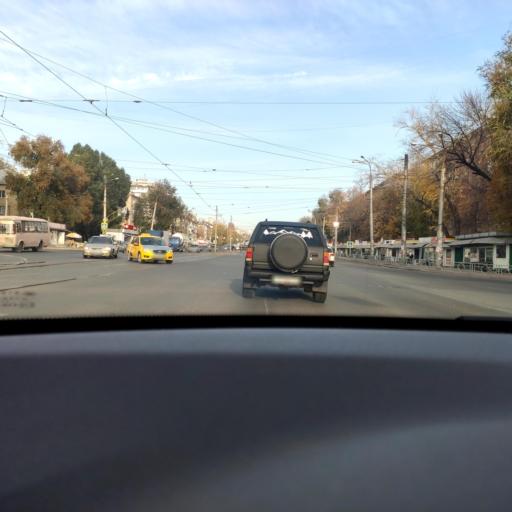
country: RU
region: Samara
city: Samara
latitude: 53.2052
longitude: 50.2370
